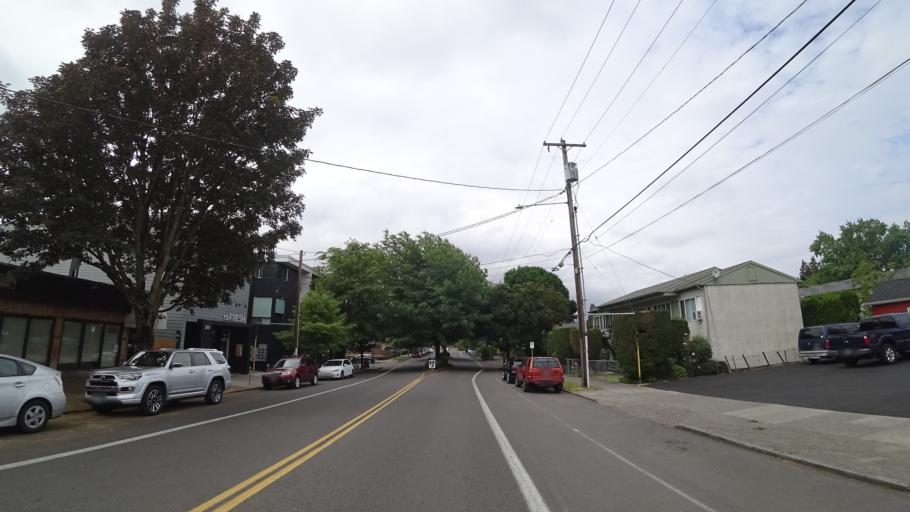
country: US
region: Oregon
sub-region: Clackamas County
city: Milwaukie
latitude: 45.4934
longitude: -122.6359
